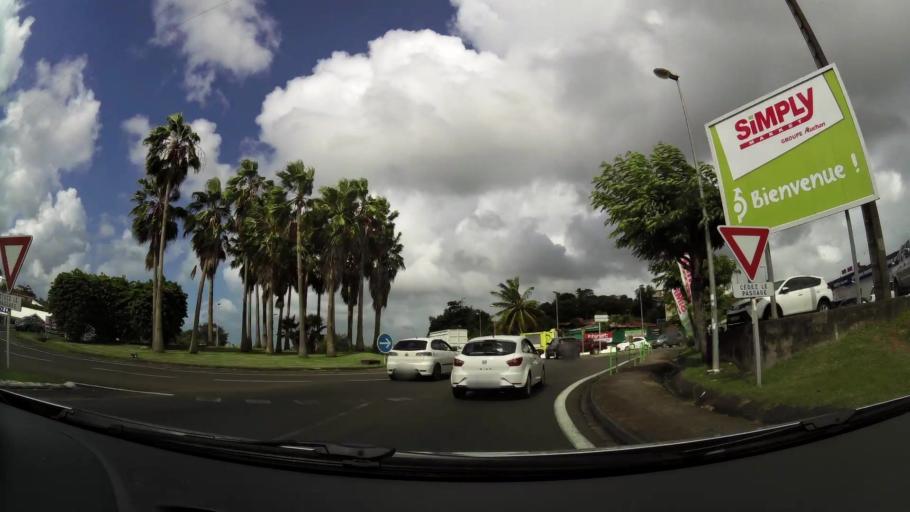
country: MQ
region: Martinique
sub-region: Martinique
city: Ducos
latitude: 14.5713
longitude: -60.9813
